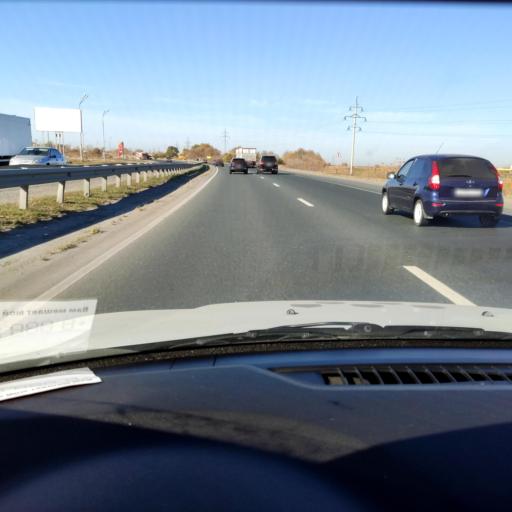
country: RU
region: Samara
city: Tol'yatti
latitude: 53.5663
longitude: 49.4931
